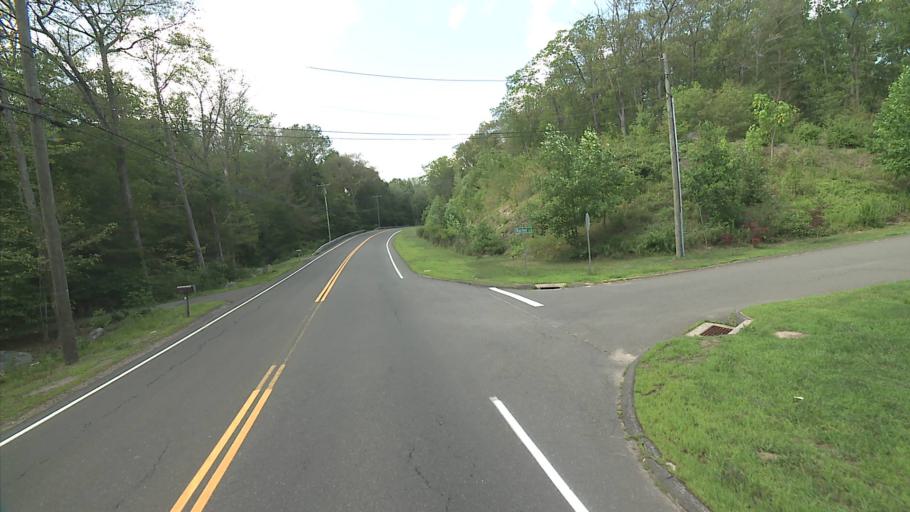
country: US
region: Connecticut
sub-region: Middlesex County
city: Higganum
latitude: 41.4123
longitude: -72.5628
